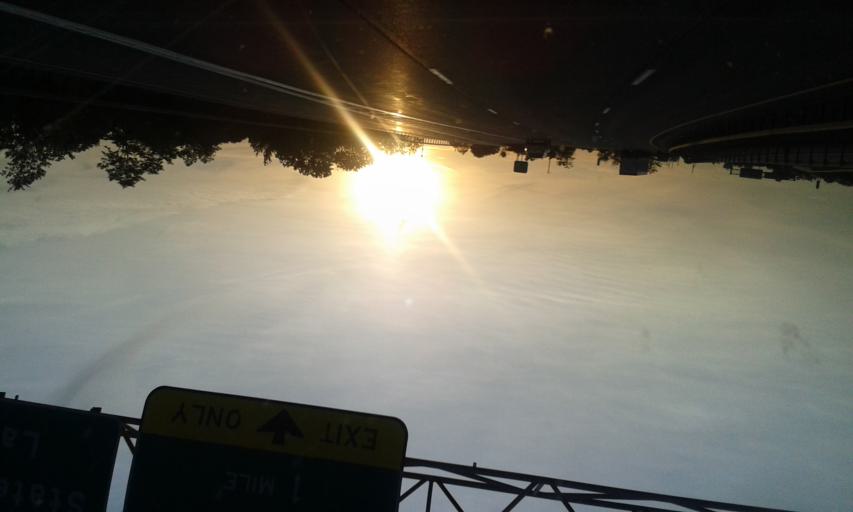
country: US
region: New York
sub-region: Onondaga County
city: Lakeland
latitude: 43.1061
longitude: -76.2476
